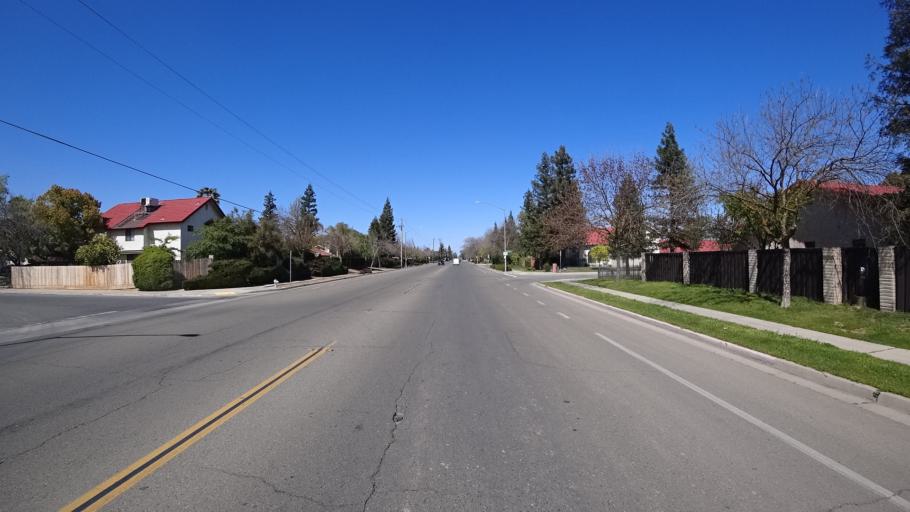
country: US
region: California
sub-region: Fresno County
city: West Park
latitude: 36.7837
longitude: -119.8623
